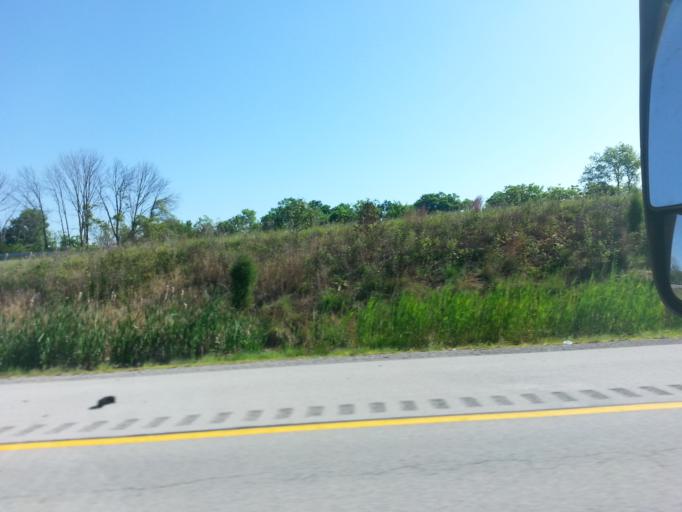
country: US
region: Kentucky
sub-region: Shelby County
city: Shelbyville
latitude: 38.1668
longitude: -85.1397
